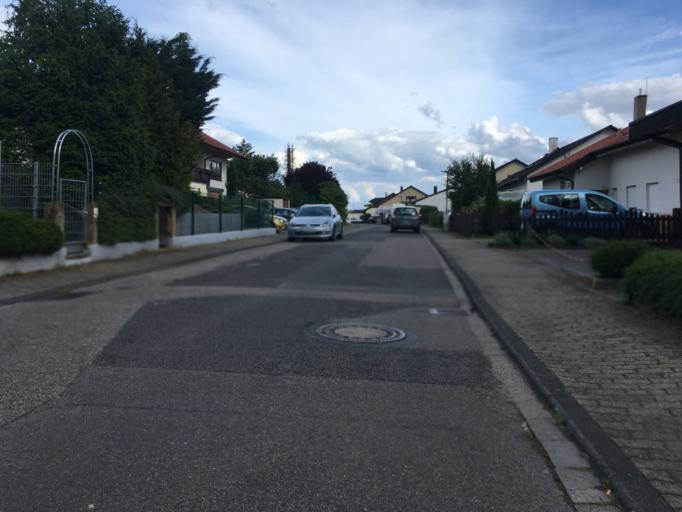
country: DE
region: Baden-Wuerttemberg
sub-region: Regierungsbezirk Stuttgart
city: Bad Rappenau
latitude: 49.2519
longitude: 9.1270
